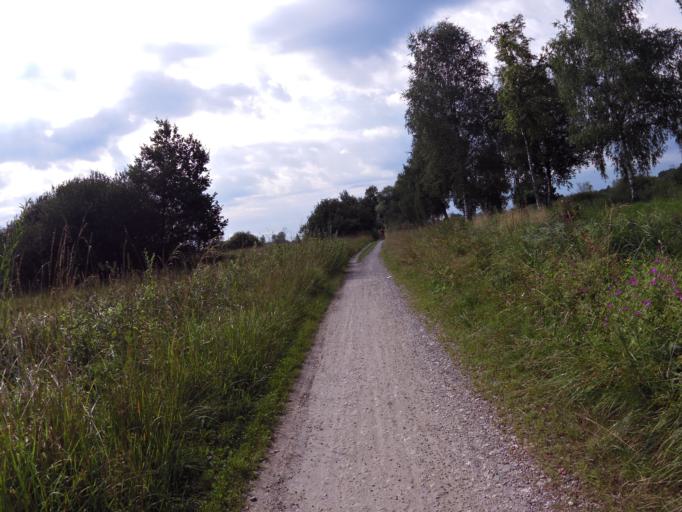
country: DE
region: Bavaria
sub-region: Upper Bavaria
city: Diessen am Ammersee
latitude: 47.9384
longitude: 11.1076
